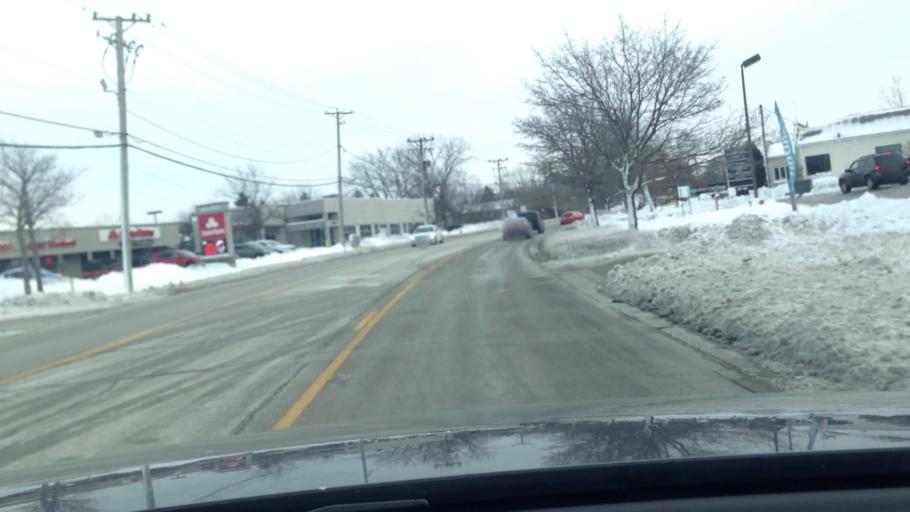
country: US
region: Illinois
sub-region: McHenry County
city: Woodstock
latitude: 42.3090
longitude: -88.4320
